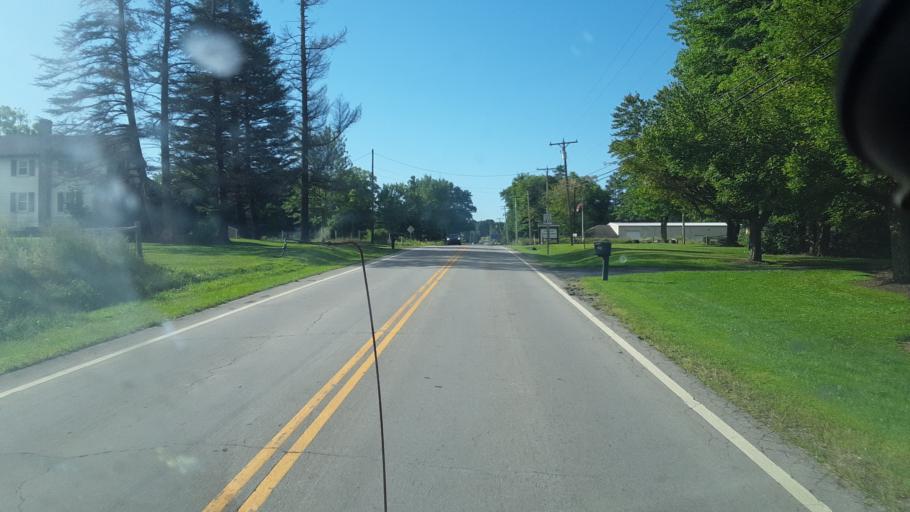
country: US
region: Ohio
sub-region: Portage County
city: Mantua
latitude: 41.3153
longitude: -81.2216
